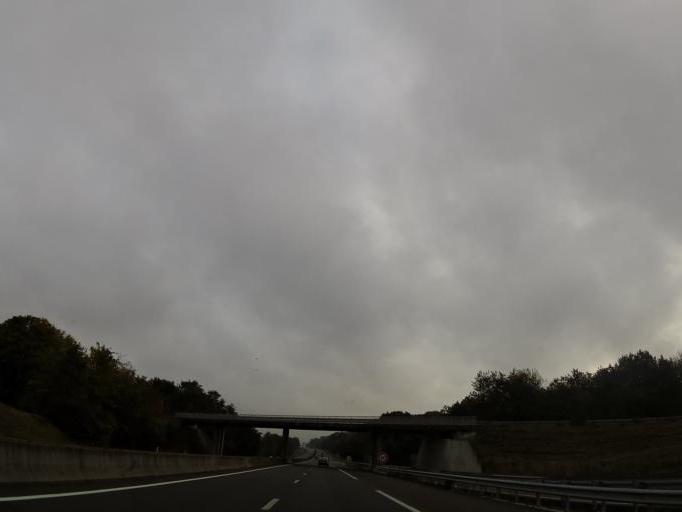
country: FR
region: Ile-de-France
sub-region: Departement de Seine-et-Marne
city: Bouleurs
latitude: 48.8854
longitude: 2.8948
